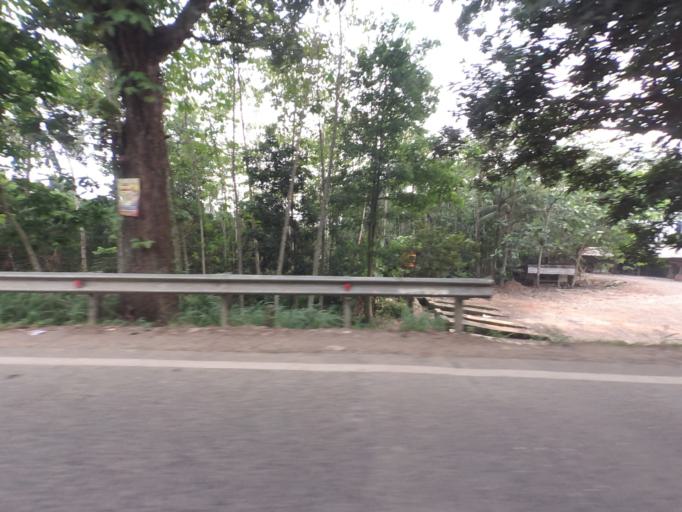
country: ID
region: West Java
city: Sidoger Lebak
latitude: -6.5650
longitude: 106.5900
